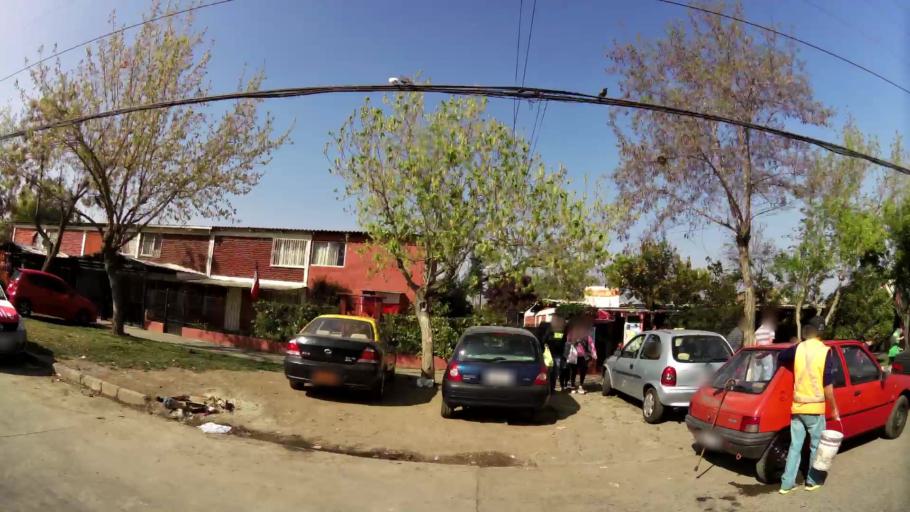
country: CL
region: Santiago Metropolitan
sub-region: Provincia de Santiago
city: Santiago
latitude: -33.4686
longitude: -70.6171
